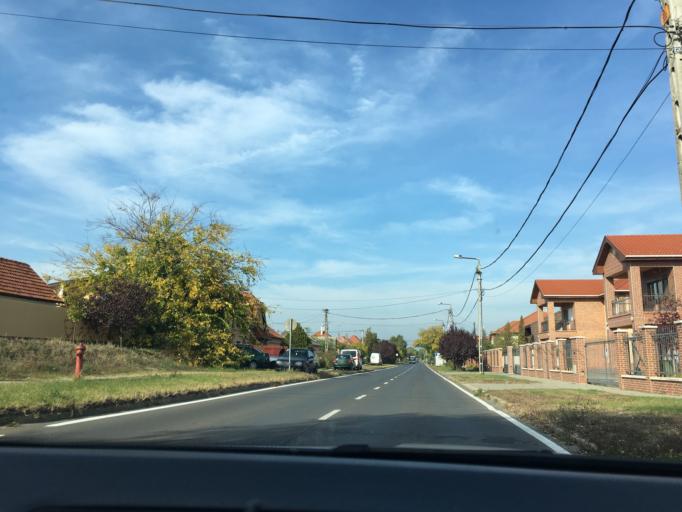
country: HU
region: Hajdu-Bihar
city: Debrecen
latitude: 47.5319
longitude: 21.6712
